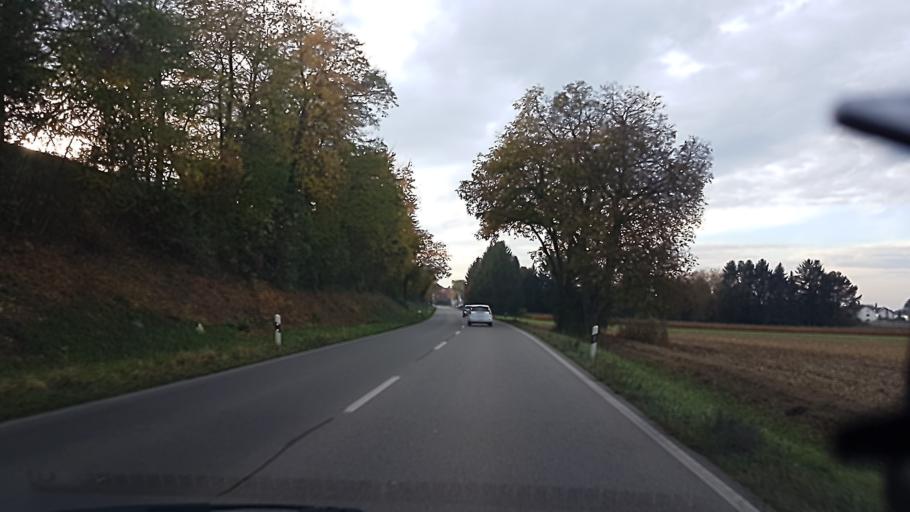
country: DE
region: Baden-Wuerttemberg
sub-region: Freiburg Region
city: Endingen
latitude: 48.1427
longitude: 7.7154
